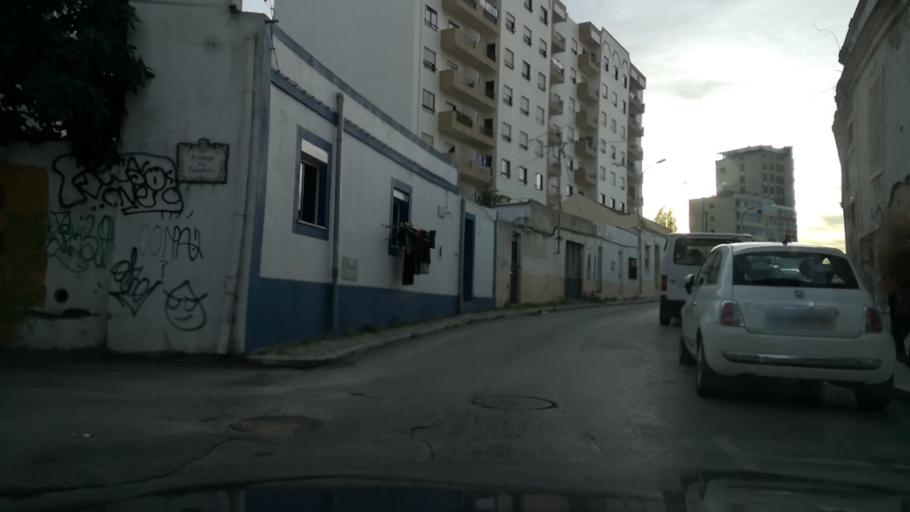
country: PT
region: Setubal
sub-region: Setubal
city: Setubal
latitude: 38.5315
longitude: -8.8773
